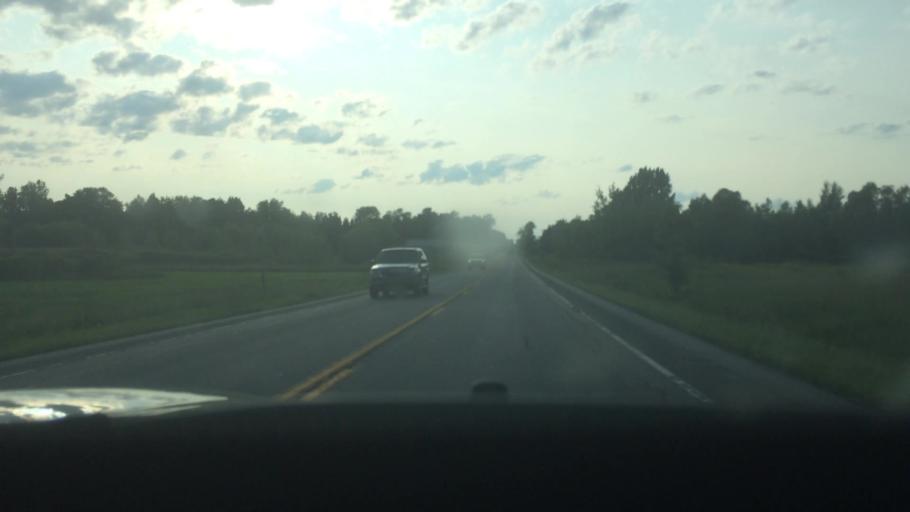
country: US
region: New York
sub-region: St. Lawrence County
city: Ogdensburg
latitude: 44.6727
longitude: -75.3928
